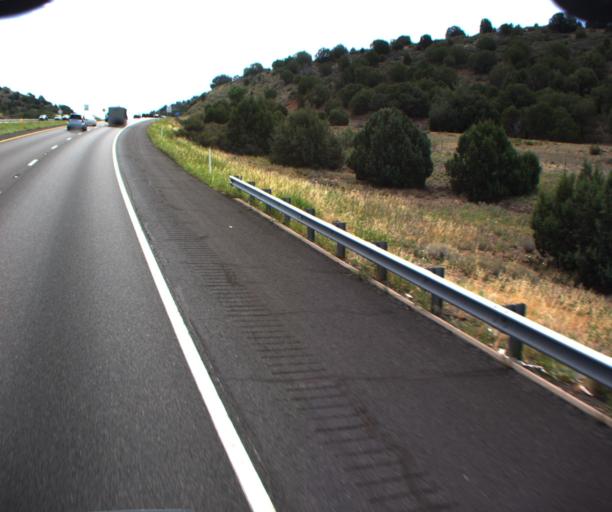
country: US
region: Arizona
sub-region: Yavapai County
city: Camp Verde
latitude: 34.5338
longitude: -111.9720
